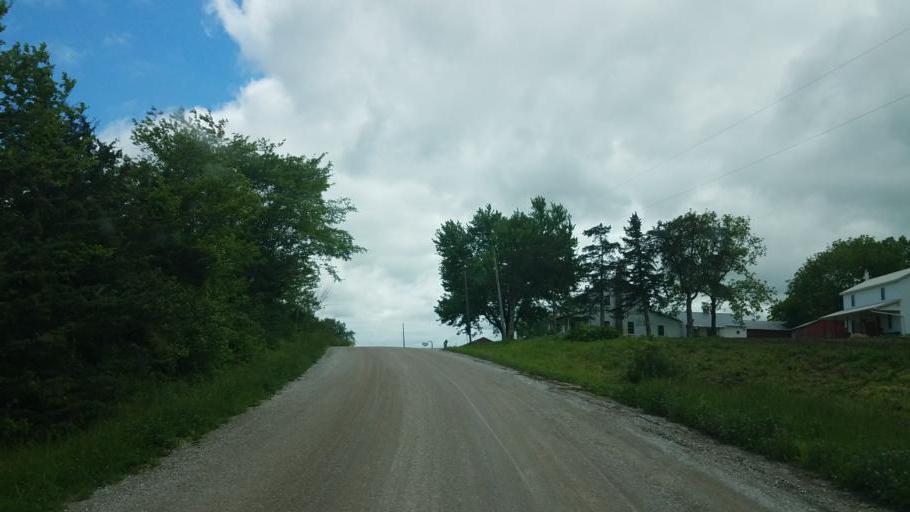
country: US
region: Iowa
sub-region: Decatur County
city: Lamoni
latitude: 40.6223
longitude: -93.8437
